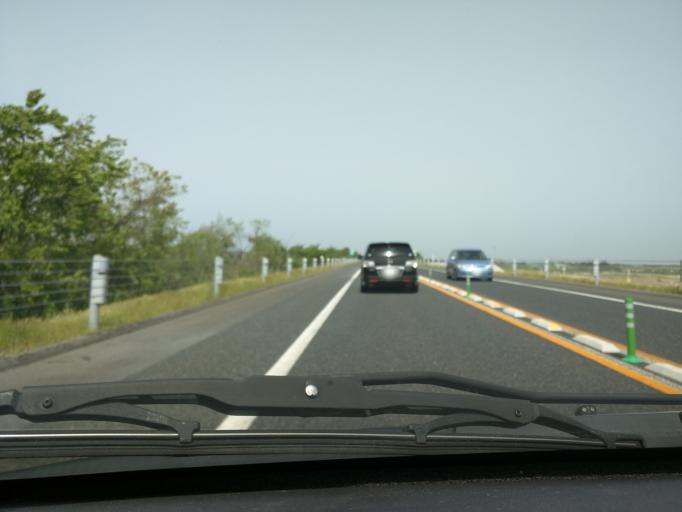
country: JP
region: Niigata
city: Gosen
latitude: 37.7766
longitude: 139.1817
